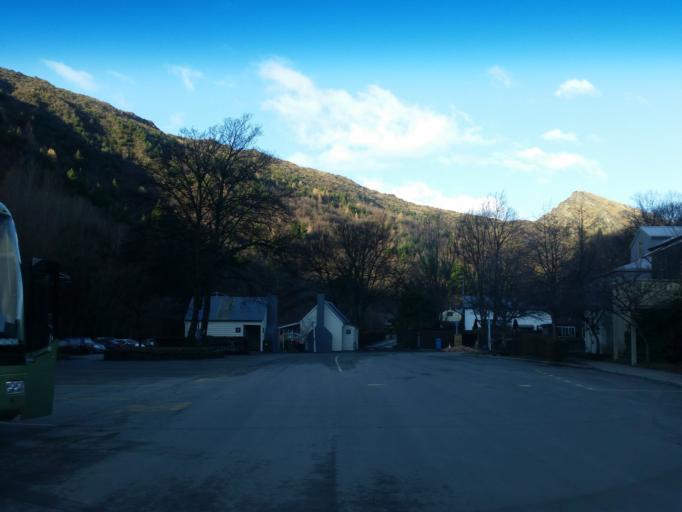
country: NZ
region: Otago
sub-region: Queenstown-Lakes District
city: Arrowtown
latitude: -44.9382
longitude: 168.8325
